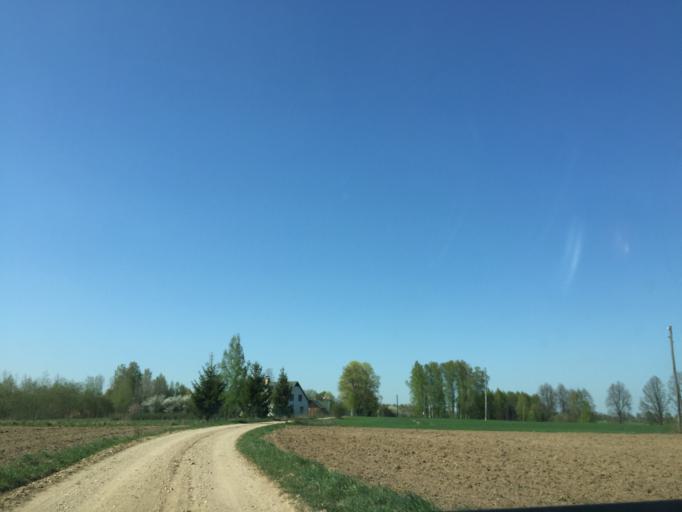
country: LV
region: Malpils
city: Malpils
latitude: 56.9332
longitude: 24.9248
